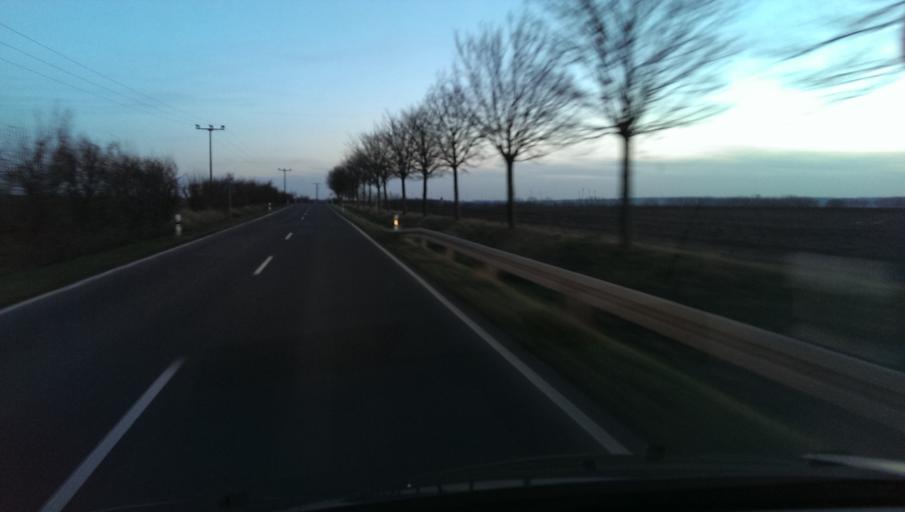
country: DE
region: Saxony-Anhalt
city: Ausleben
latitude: 52.0544
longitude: 11.0872
